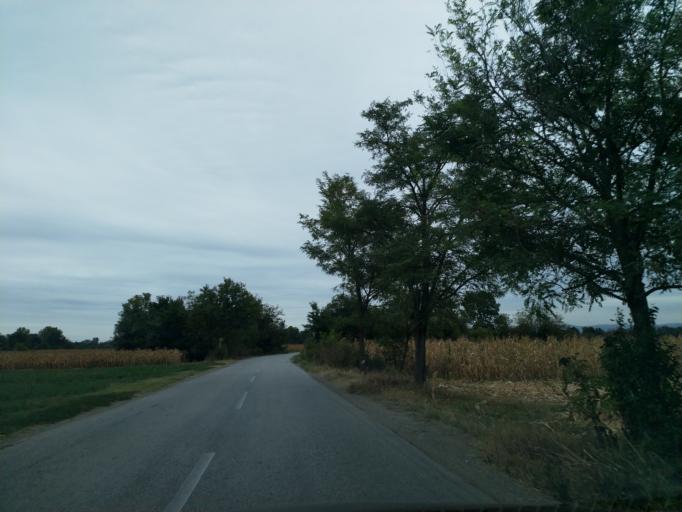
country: RS
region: Central Serbia
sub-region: Pomoravski Okrug
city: Paracin
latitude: 43.8371
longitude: 21.3700
